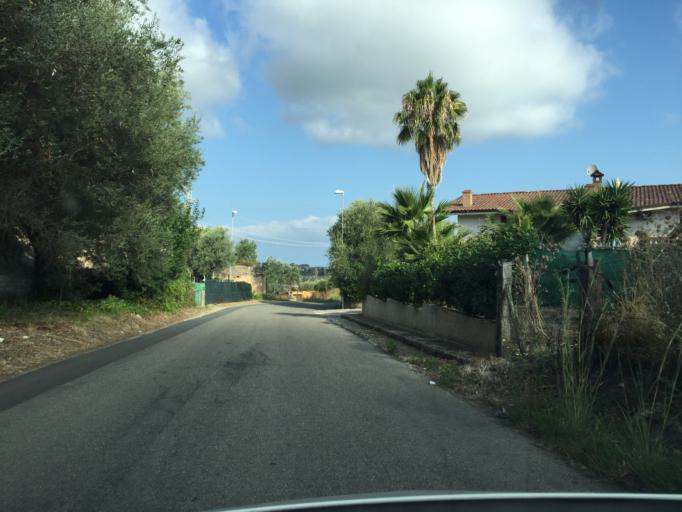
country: IT
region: Calabria
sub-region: Provincia di Vibo-Valentia
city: Pannaconi
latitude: 38.6983
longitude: 16.0457
